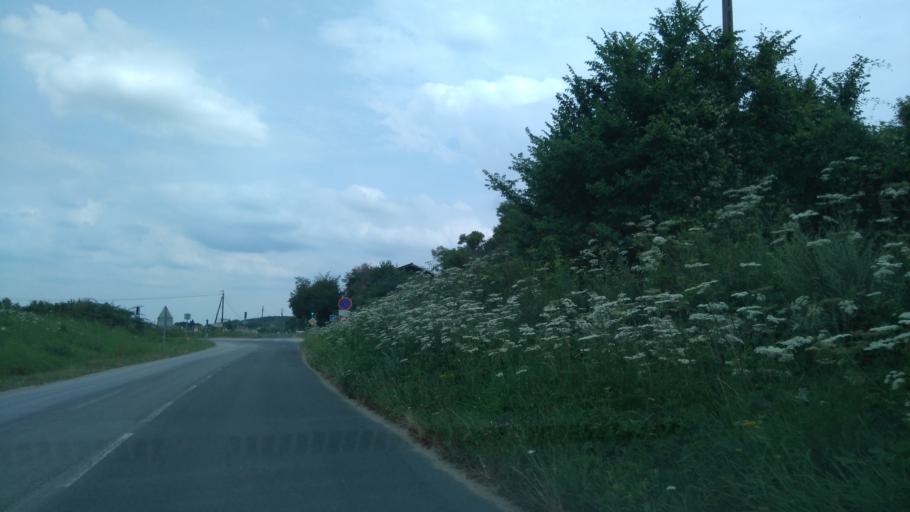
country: FR
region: Picardie
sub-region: Departement de l'Oise
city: Saint-Maximin
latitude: 49.2146
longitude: 2.4325
